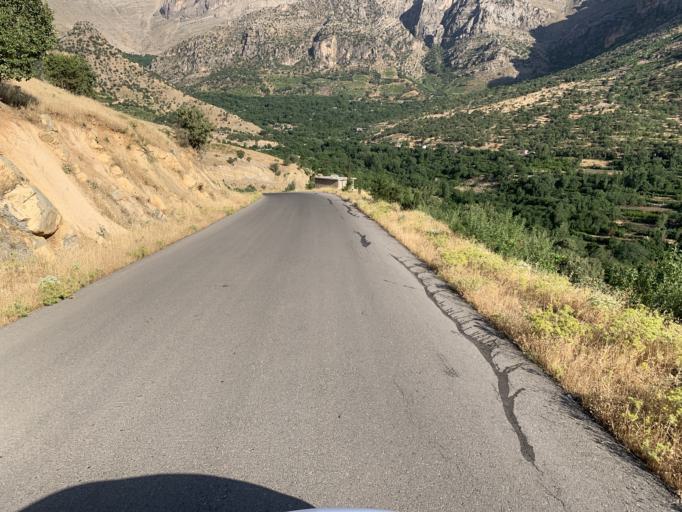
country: IQ
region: As Sulaymaniyah
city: Qeladize
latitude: 35.9952
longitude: 45.1925
